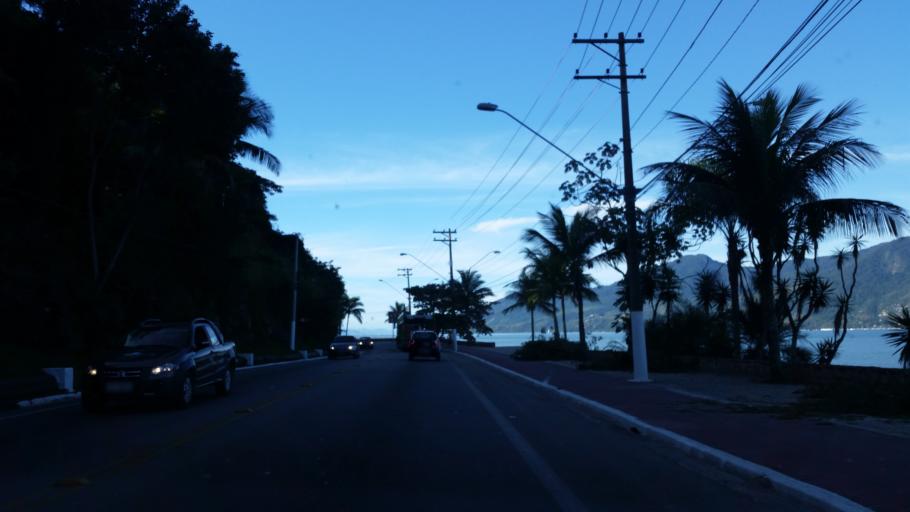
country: BR
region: Sao Paulo
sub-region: Sao Sebastiao
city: Sao Sebastiao
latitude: -23.7835
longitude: -45.3986
